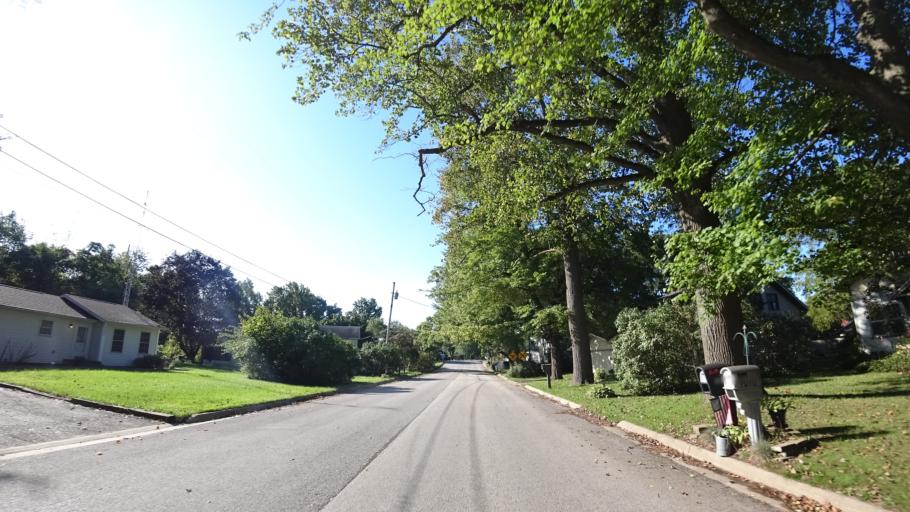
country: US
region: Michigan
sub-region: Berrien County
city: Lake Michigan Beach
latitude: 42.1849
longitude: -86.3812
